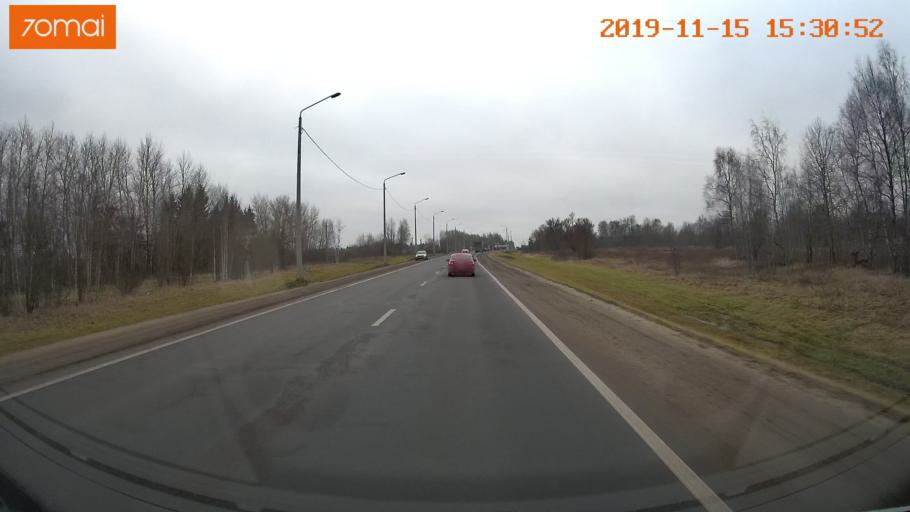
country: RU
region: Jaroslavl
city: Danilov
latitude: 58.1058
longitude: 40.1110
